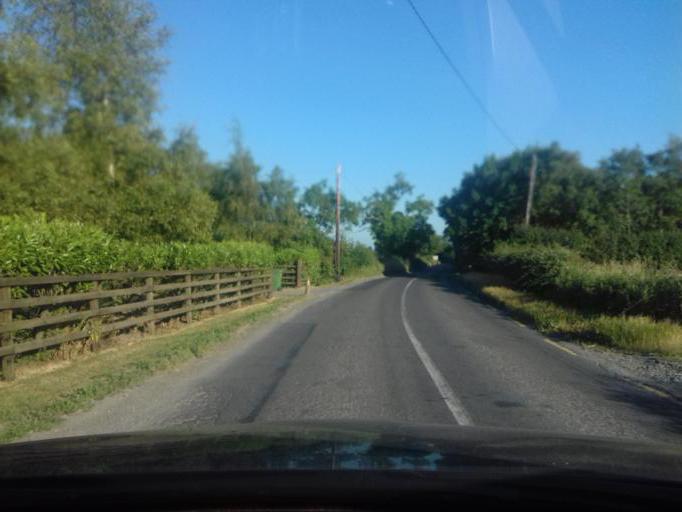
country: IE
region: Leinster
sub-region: Dublin City
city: Finglas
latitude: 53.4436
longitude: -6.3015
